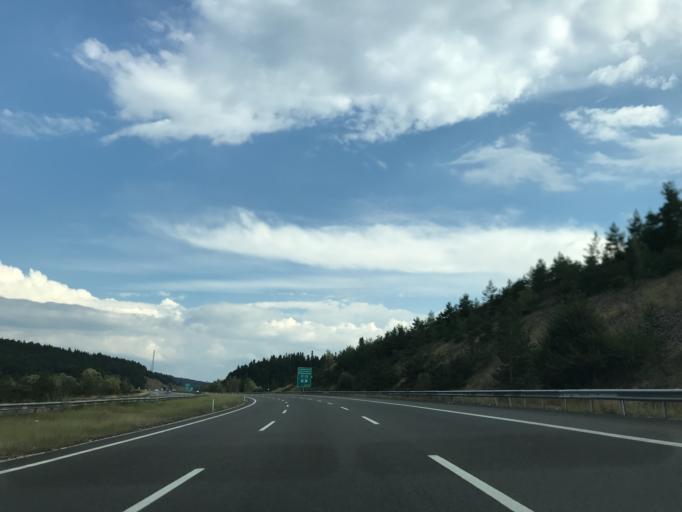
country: TR
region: Bolu
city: Gerede
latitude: 40.6231
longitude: 32.2386
